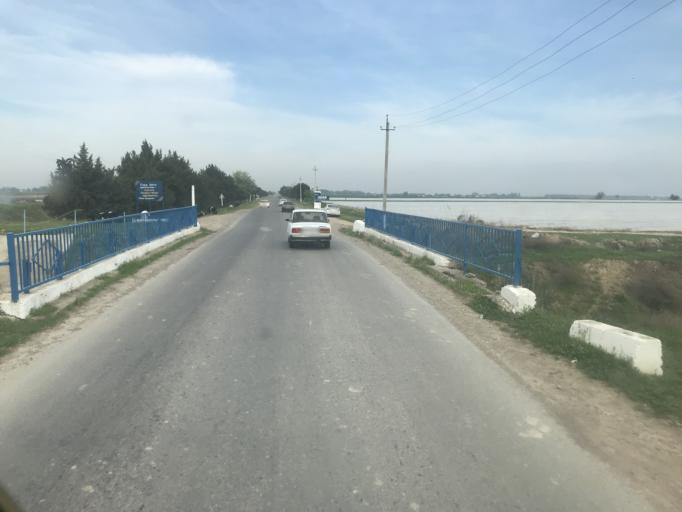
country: KZ
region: Ongtustik Qazaqstan
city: Asykata
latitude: 40.9841
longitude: 68.2966
